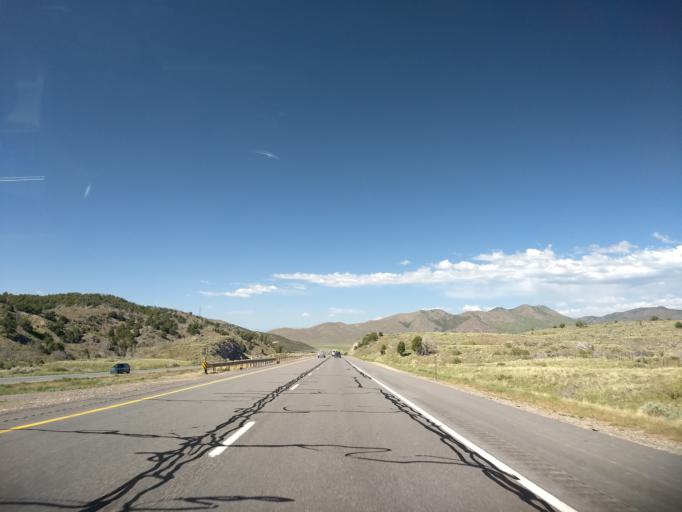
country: US
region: Utah
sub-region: Beaver County
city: Beaver
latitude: 38.6400
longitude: -112.6072
